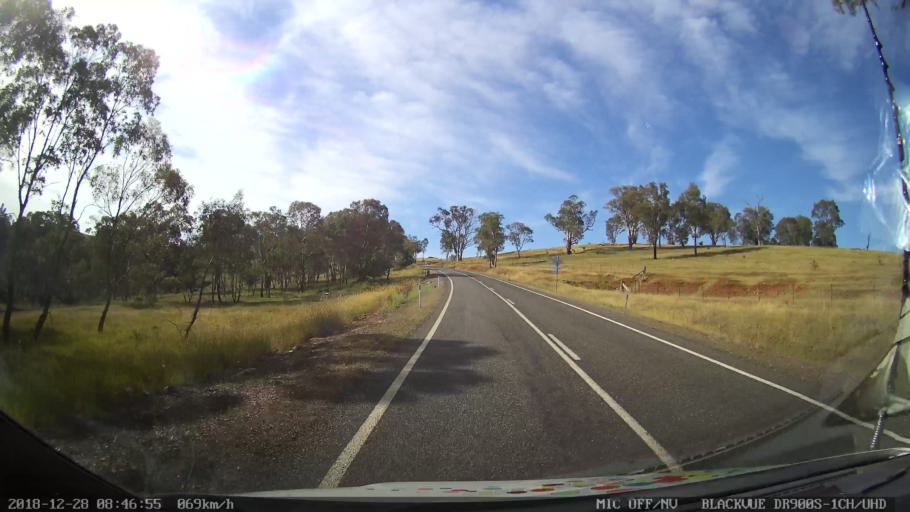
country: AU
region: New South Wales
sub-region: Upper Lachlan Shire
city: Crookwell
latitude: -34.0235
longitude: 149.3330
